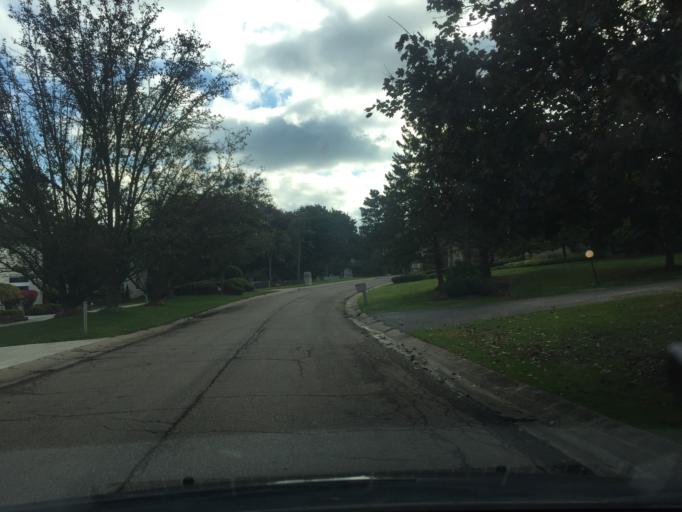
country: US
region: Michigan
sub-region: Oakland County
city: Sylvan Lake
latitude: 42.5889
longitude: -83.3127
